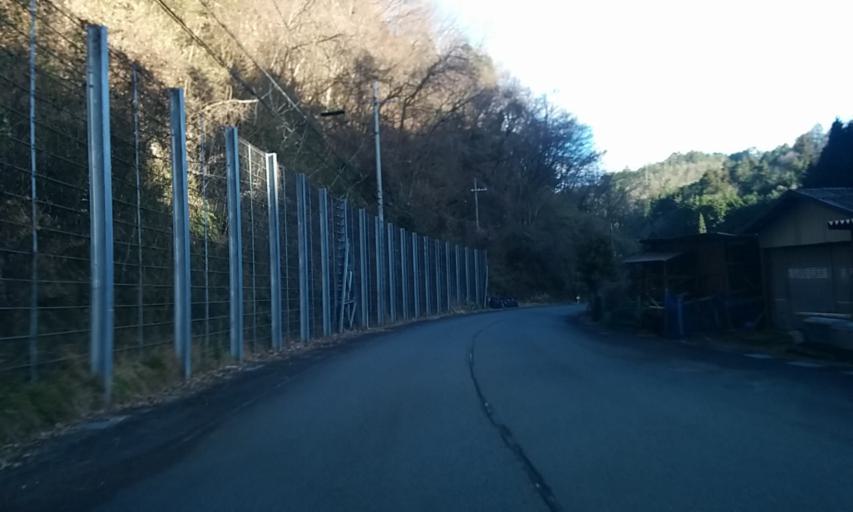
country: JP
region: Kyoto
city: Fukuchiyama
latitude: 35.2765
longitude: 135.0221
